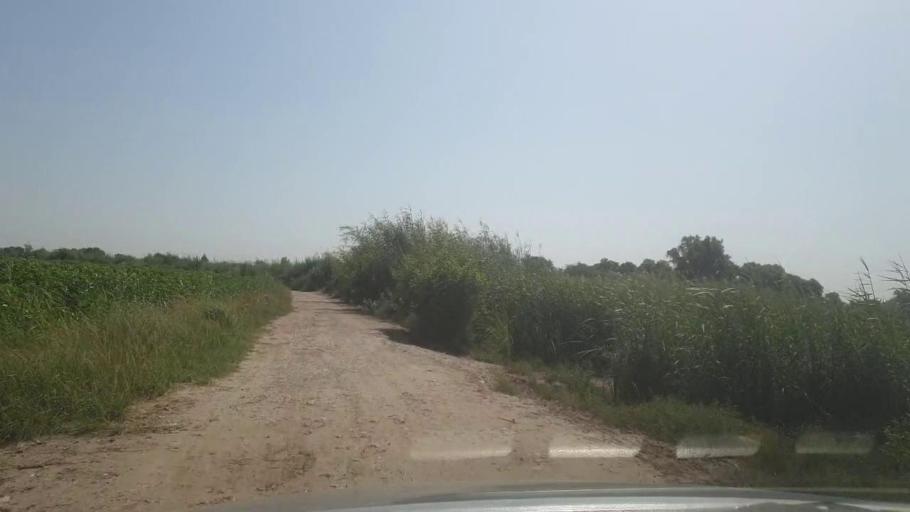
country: PK
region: Sindh
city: Rohri
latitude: 27.4066
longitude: 69.0841
